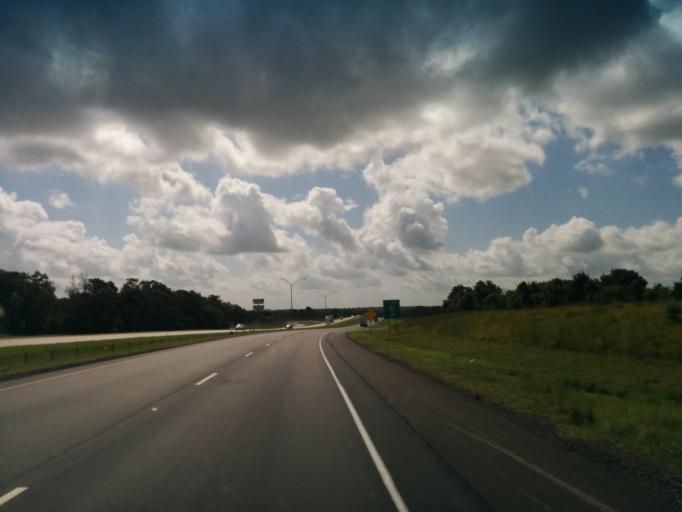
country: US
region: Texas
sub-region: Fayette County
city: Schulenburg
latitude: 29.6961
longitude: -96.8545
